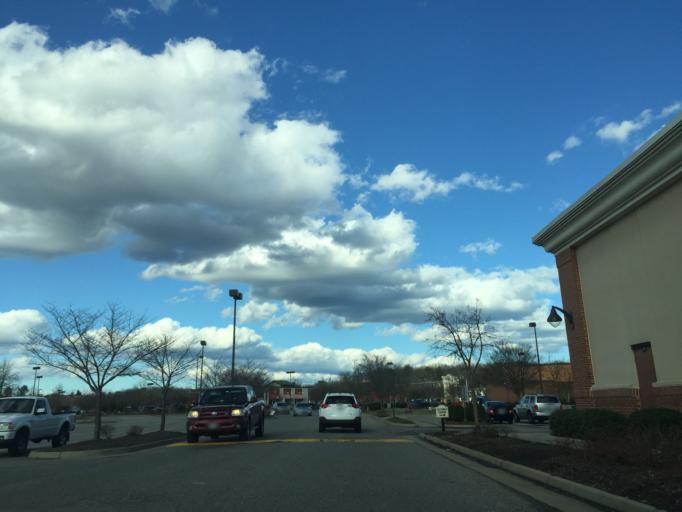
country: US
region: Virginia
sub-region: York County
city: Yorktown
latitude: 37.1295
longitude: -76.5153
